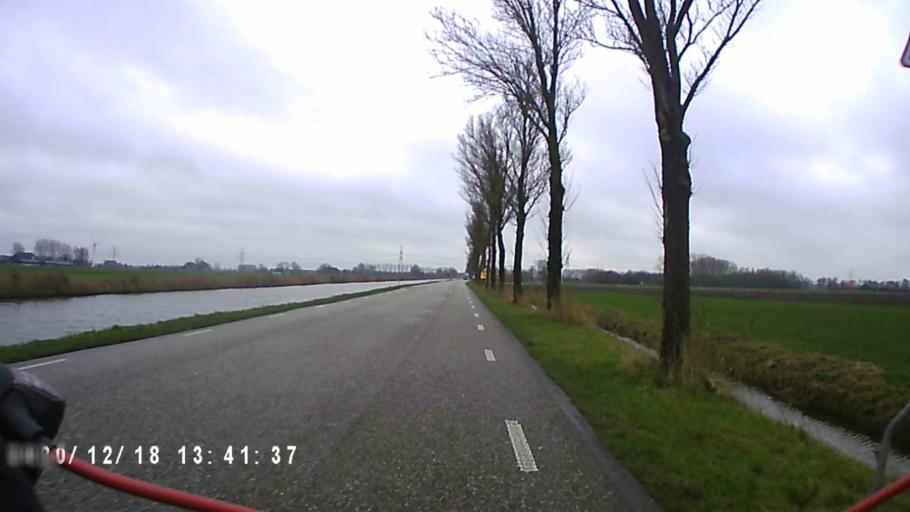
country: NL
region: Groningen
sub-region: Gemeente Bedum
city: Bedum
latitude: 53.3203
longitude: 6.5962
